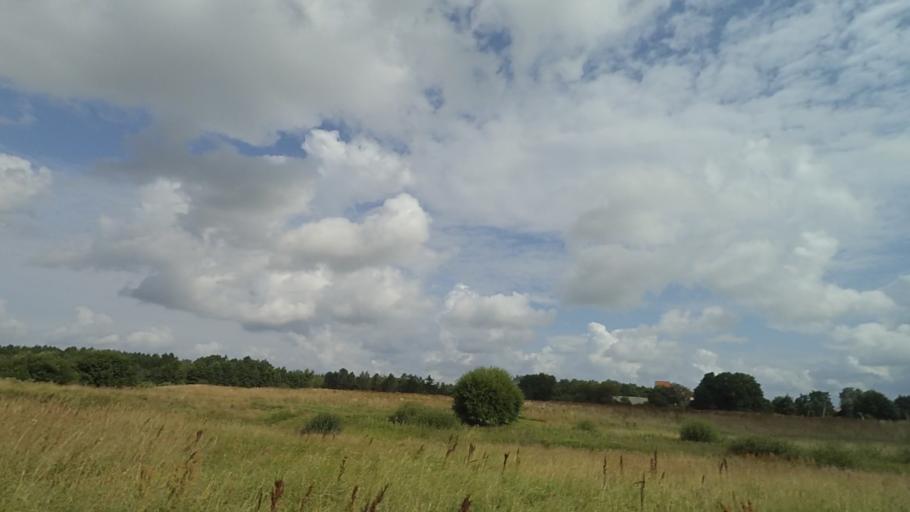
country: DK
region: Central Jutland
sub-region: Syddjurs Kommune
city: Ryomgard
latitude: 56.4774
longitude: 10.5016
